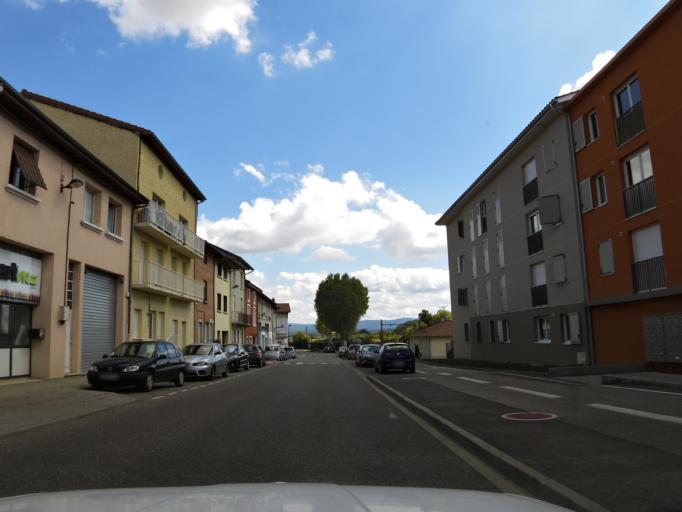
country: FR
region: Rhone-Alpes
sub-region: Departement de l'Ain
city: Meximieux
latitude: 45.9047
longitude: 5.1997
